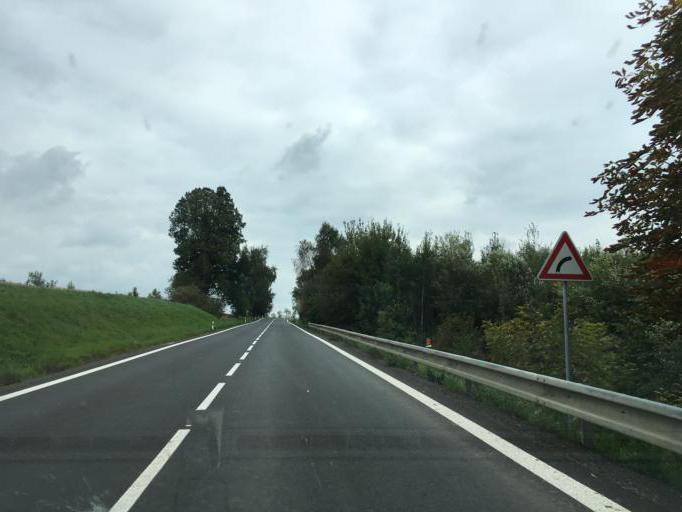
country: CZ
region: Central Bohemia
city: Cechtice
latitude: 49.5633
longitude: 15.1116
